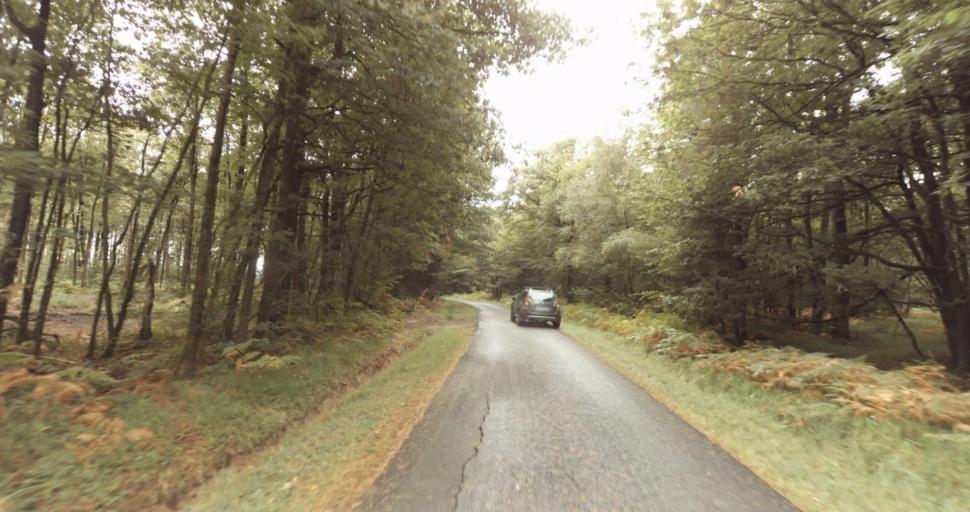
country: FR
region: Lower Normandy
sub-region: Departement de l'Orne
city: Sainte-Gauburge-Sainte-Colombe
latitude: 48.7540
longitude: 0.4726
